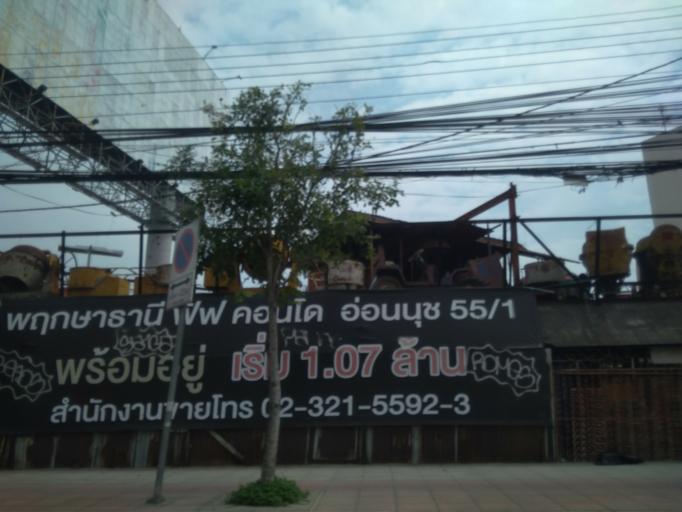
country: TH
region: Bangkok
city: Suan Luang
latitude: 13.7315
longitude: 100.6414
